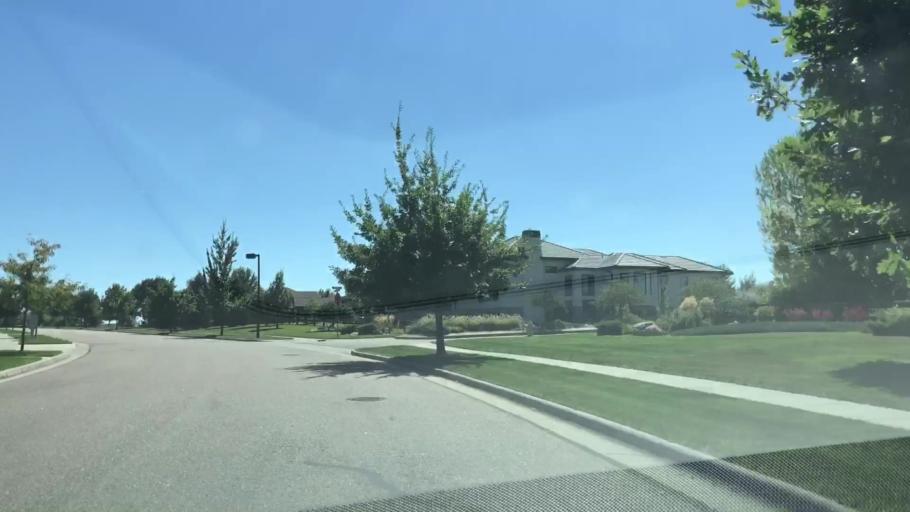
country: US
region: Colorado
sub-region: Weld County
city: Windsor
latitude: 40.5332
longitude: -104.9576
